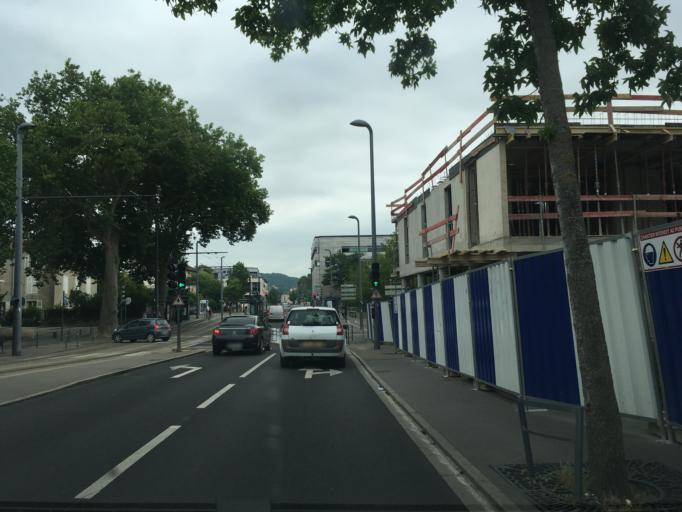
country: FR
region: Lorraine
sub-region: Departement de Meurthe-et-Moselle
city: Nancy
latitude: 48.6952
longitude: 6.1946
